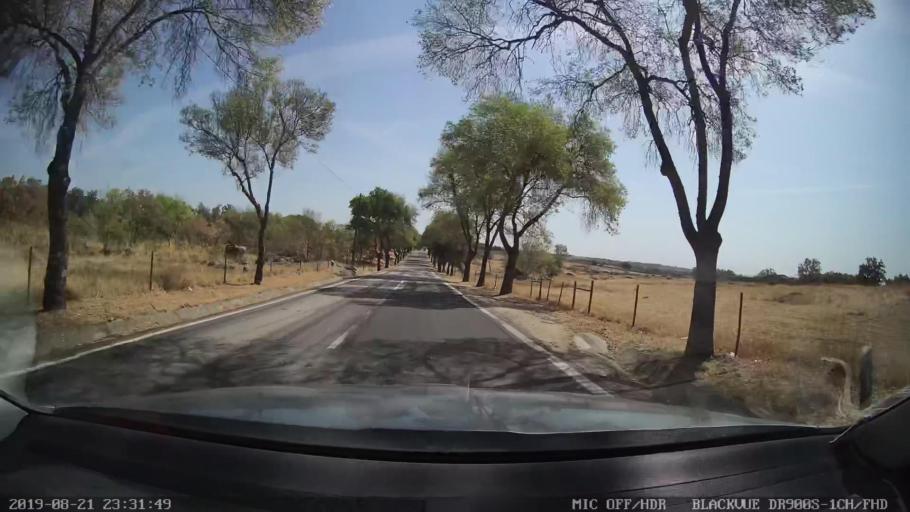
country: PT
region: Guarda
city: Alcains
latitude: 39.8750
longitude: -7.4236
